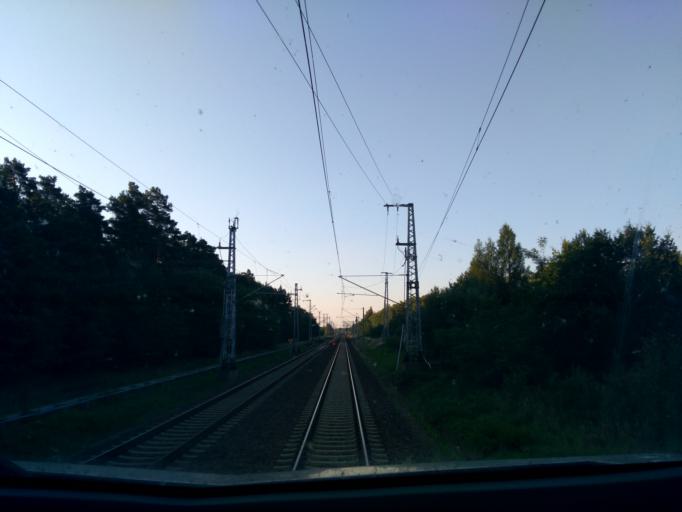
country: DE
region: Brandenburg
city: Halbe
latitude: 52.1174
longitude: 13.6922
